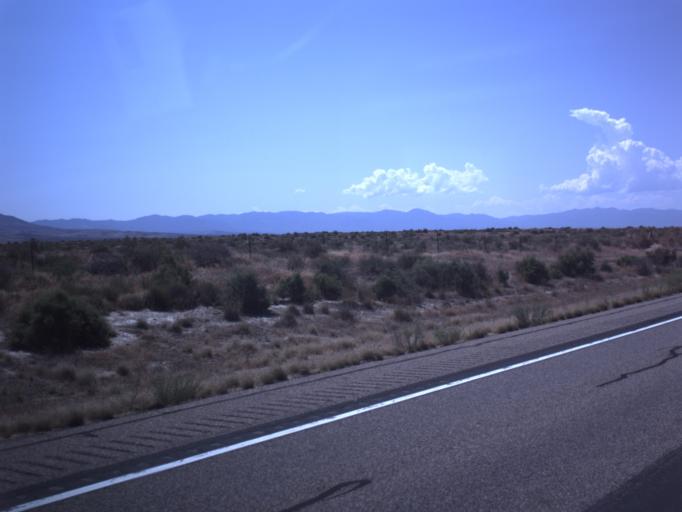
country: US
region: Utah
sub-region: Millard County
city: Delta
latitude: 39.3689
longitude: -112.4965
